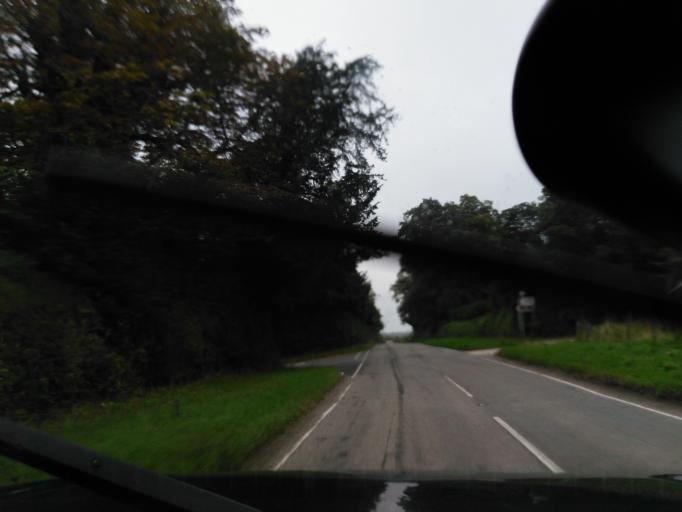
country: GB
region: England
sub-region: Dorset
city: Blandford Forum
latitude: 50.9105
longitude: -2.1947
